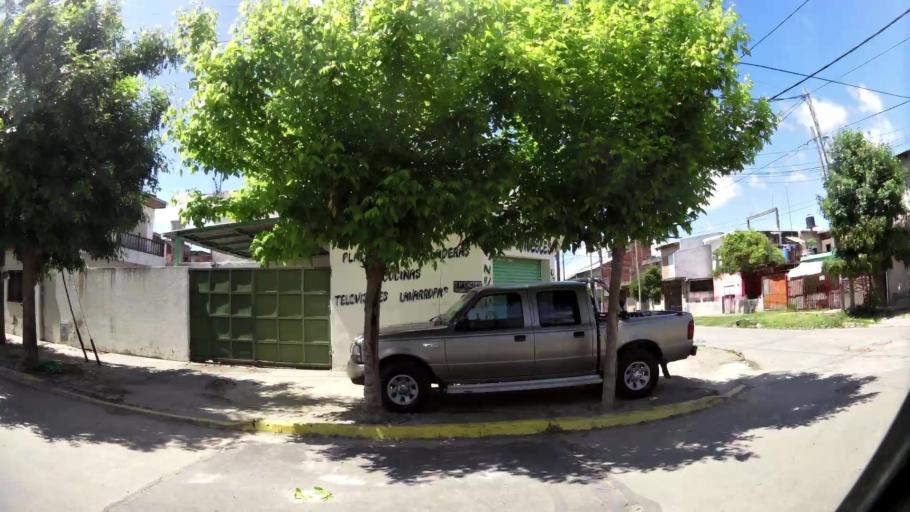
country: AR
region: Buenos Aires
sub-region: Partido de Lanus
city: Lanus
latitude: -34.6928
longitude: -58.4333
